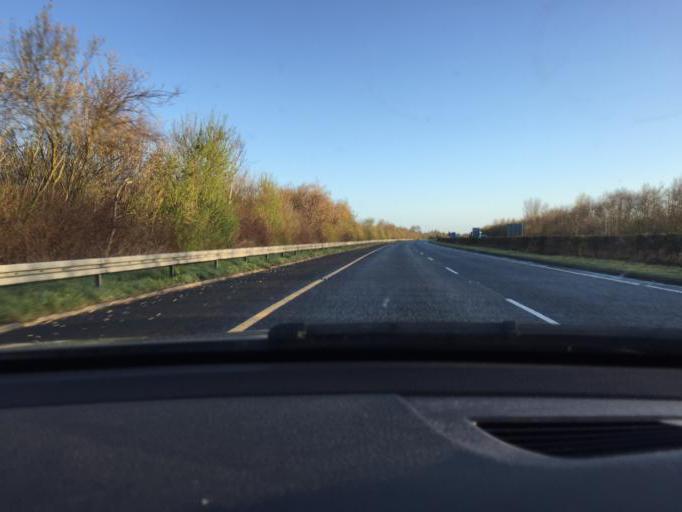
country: IE
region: Leinster
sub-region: Lu
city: Castlebellingham
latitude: 53.8809
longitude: -6.4301
